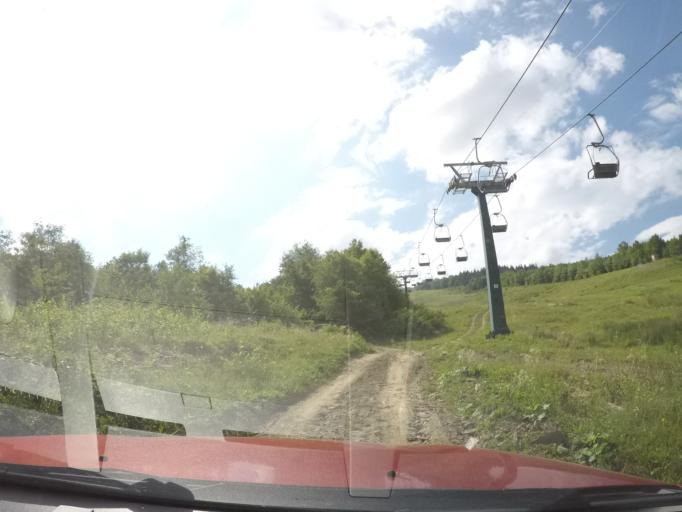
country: UA
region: Zakarpattia
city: Velykyi Bereznyi
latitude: 48.9489
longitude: 22.6611
